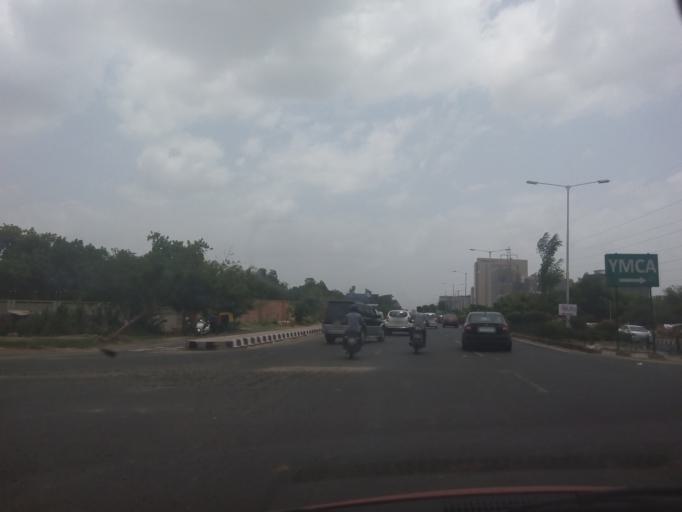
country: IN
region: Gujarat
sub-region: Ahmadabad
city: Sarkhej
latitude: 23.0082
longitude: 72.5013
